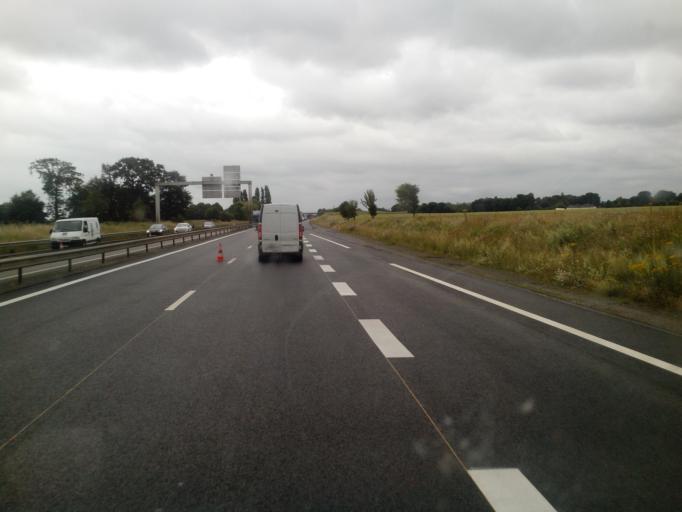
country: FR
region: Brittany
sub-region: Departement d'Ille-et-Vilaine
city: Rennes
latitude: 48.0760
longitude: -1.6755
